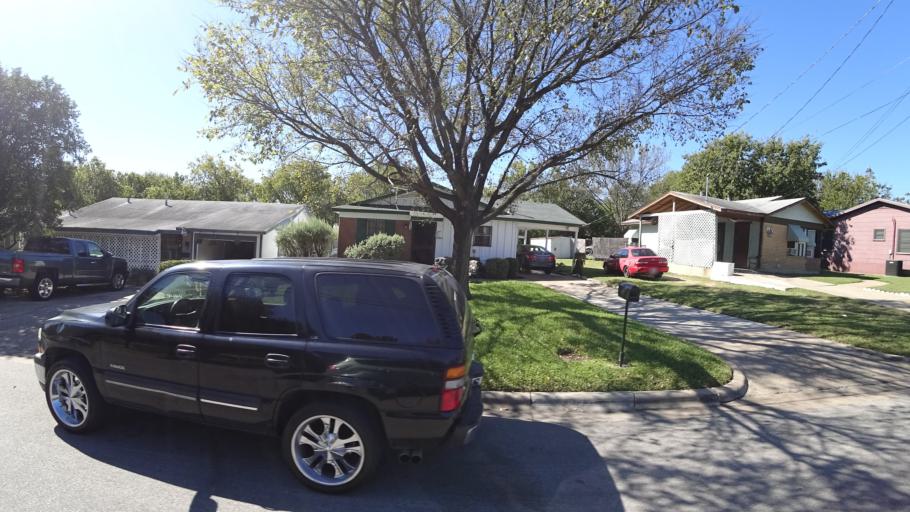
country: US
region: Texas
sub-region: Travis County
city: Austin
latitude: 30.2837
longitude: -97.6831
